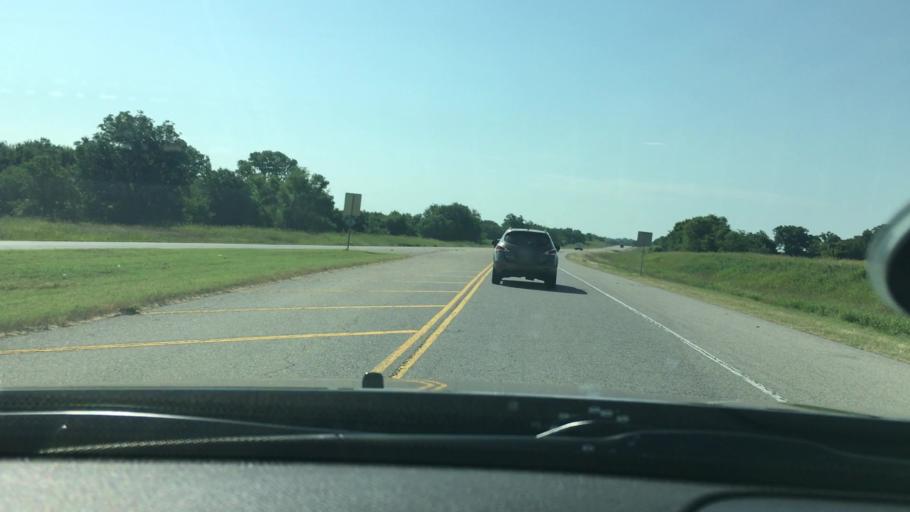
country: US
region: Oklahoma
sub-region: Pontotoc County
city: Ada
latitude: 34.7195
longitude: -96.6275
